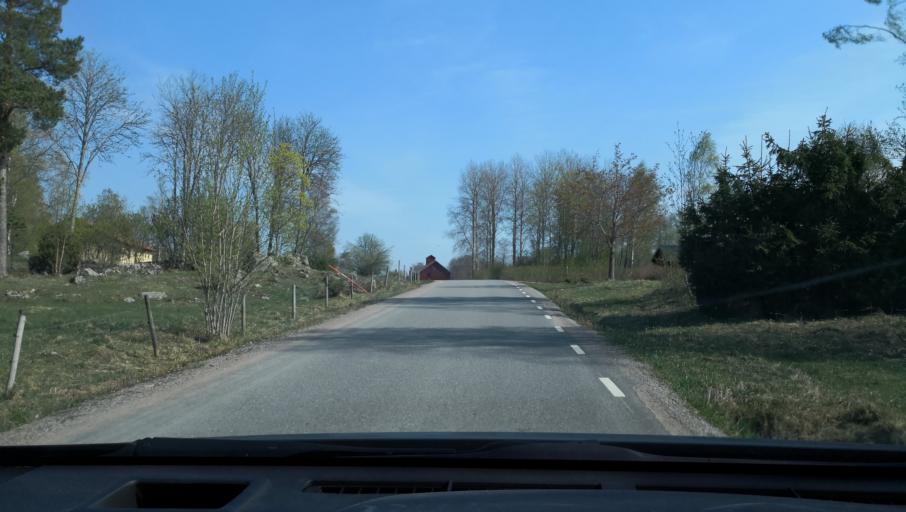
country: SE
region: Vaestmanland
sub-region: Sala Kommun
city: Sala
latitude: 60.0082
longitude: 16.6894
